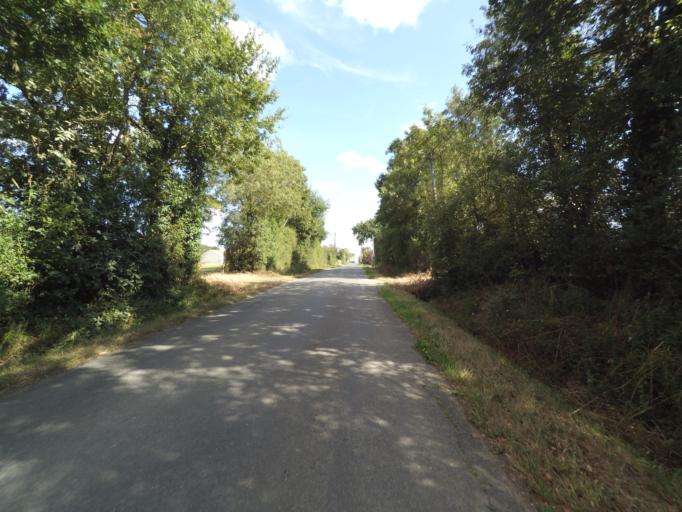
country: FR
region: Pays de la Loire
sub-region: Departement de la Loire-Atlantique
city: Vieillevigne
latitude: 46.9620
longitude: -1.4593
